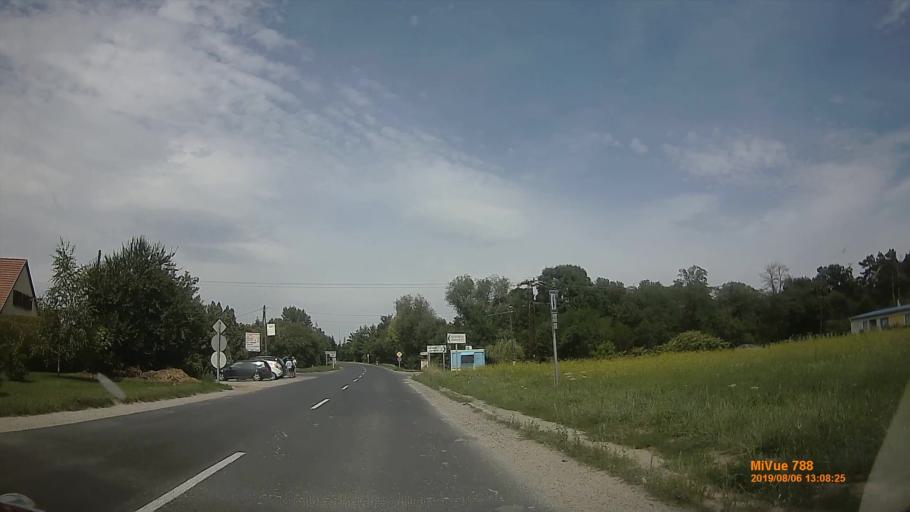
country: HU
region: Vas
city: Koszeg
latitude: 47.3887
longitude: 16.5547
